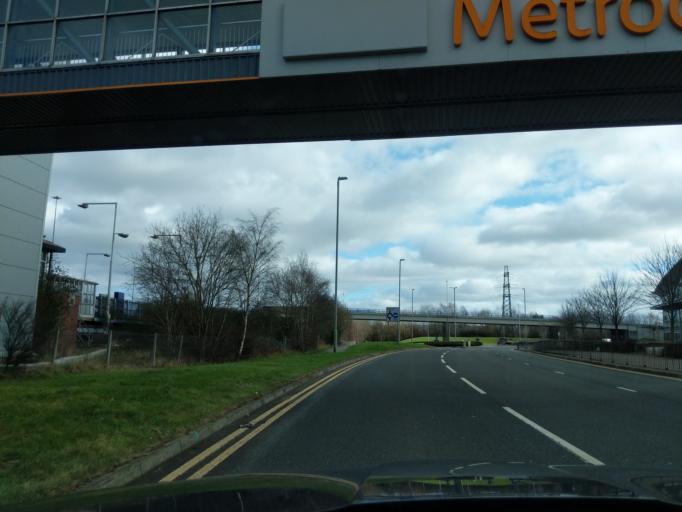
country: GB
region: England
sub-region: Newcastle upon Tyne
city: Benwell
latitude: 54.9588
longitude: -1.6657
